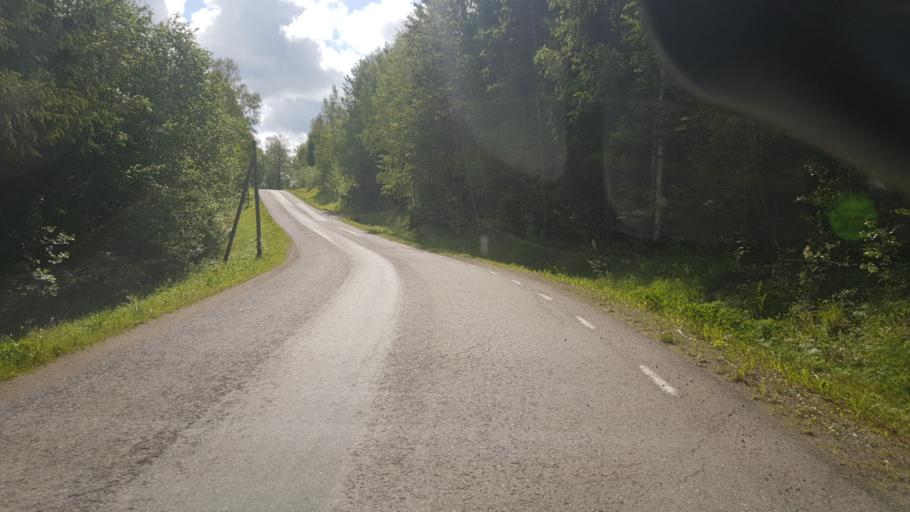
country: NO
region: Ostfold
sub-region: Romskog
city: Romskog
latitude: 59.8257
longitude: 11.9664
